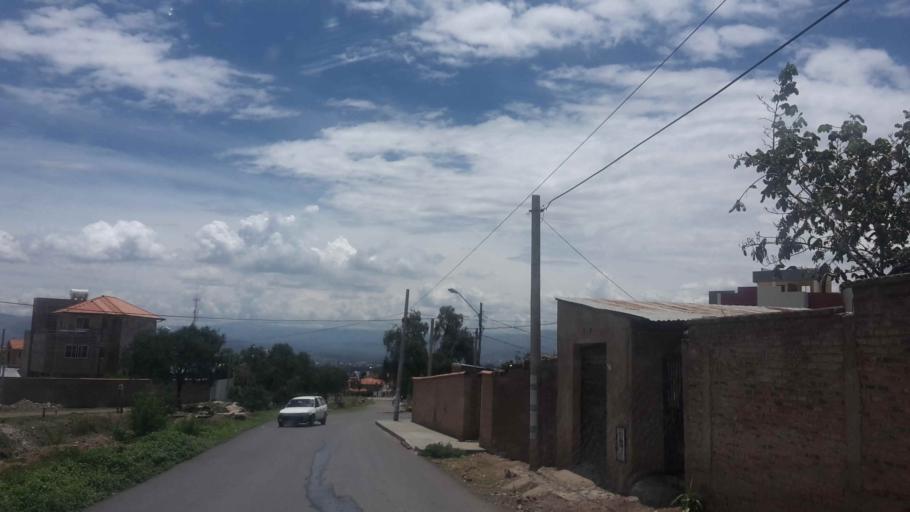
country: BO
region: Cochabamba
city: Cochabamba
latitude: -17.3482
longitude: -66.1811
